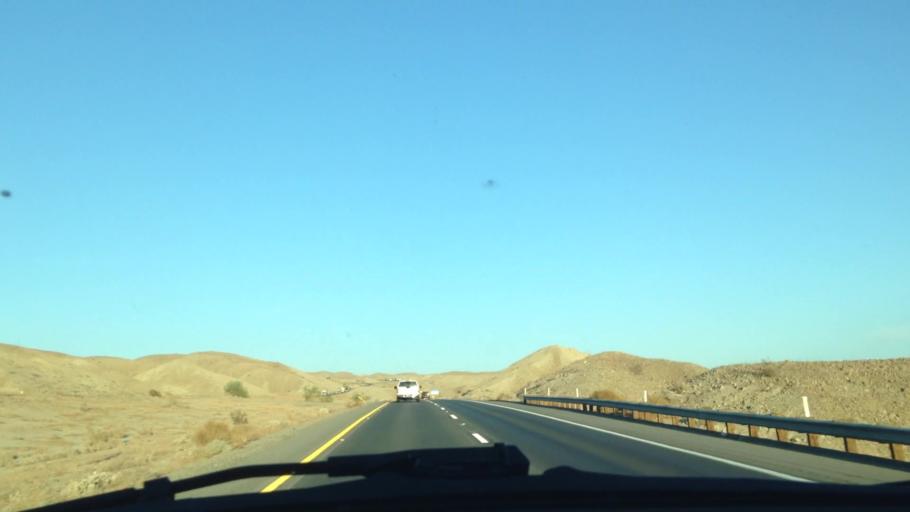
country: US
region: California
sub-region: Riverside County
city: Coachella
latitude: 33.7014
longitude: -116.1211
